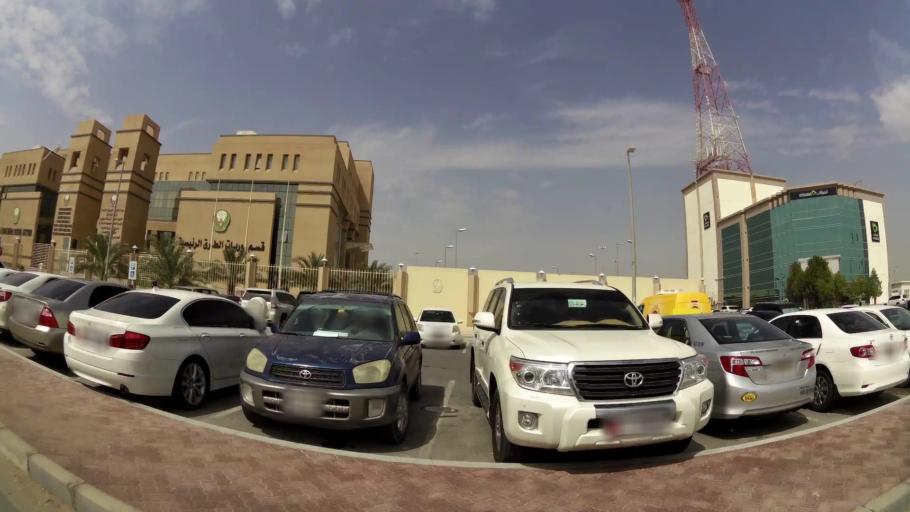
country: AE
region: Abu Dhabi
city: Abu Dhabi
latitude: 24.3115
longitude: 54.6058
